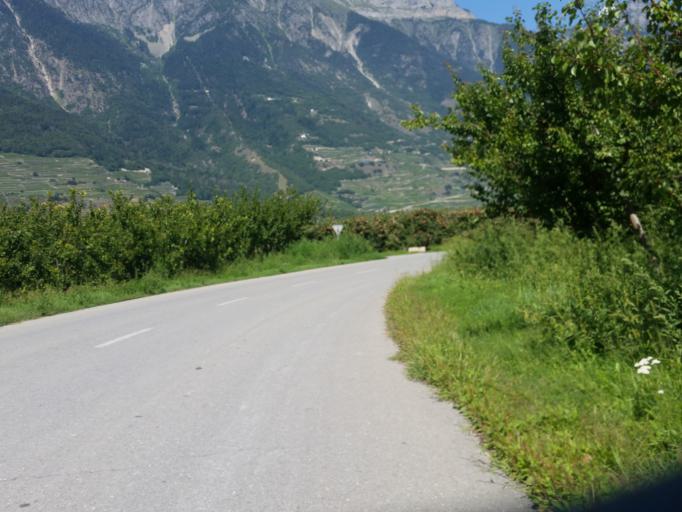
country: CH
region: Valais
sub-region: Martigny District
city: Fully
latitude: 46.1244
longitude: 7.1131
